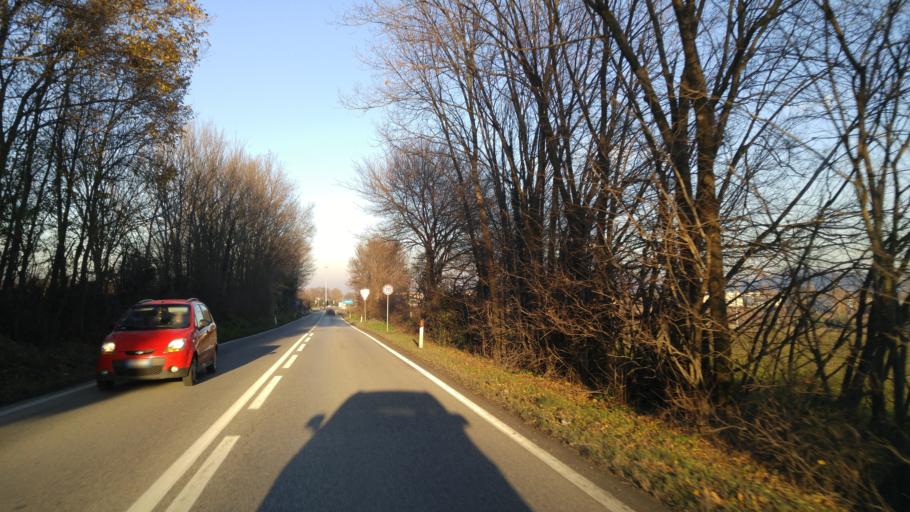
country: IT
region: The Marches
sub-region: Provincia di Ancona
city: Monterado
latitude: 43.7078
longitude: 13.0717
